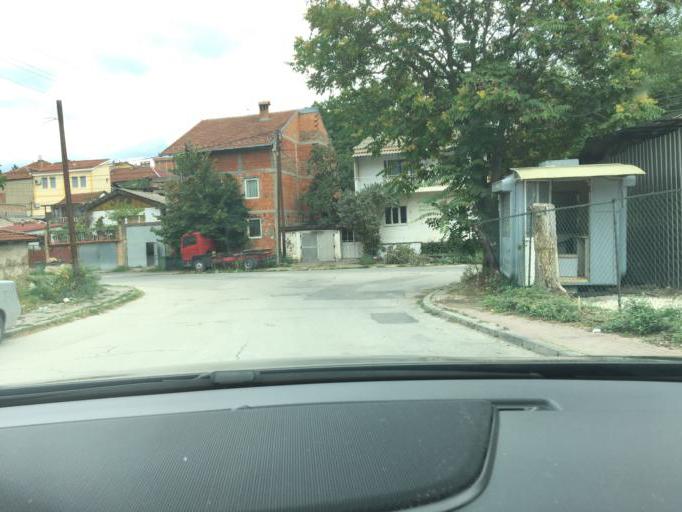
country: MK
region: Cair
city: Cair
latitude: 42.0003
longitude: 21.4481
